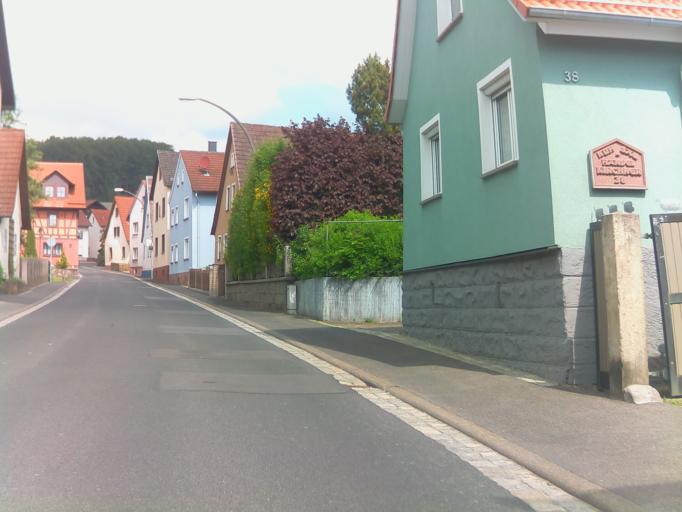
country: DE
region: Bavaria
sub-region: Regierungsbezirk Unterfranken
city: Burkardroth
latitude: 50.2710
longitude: 9.9916
